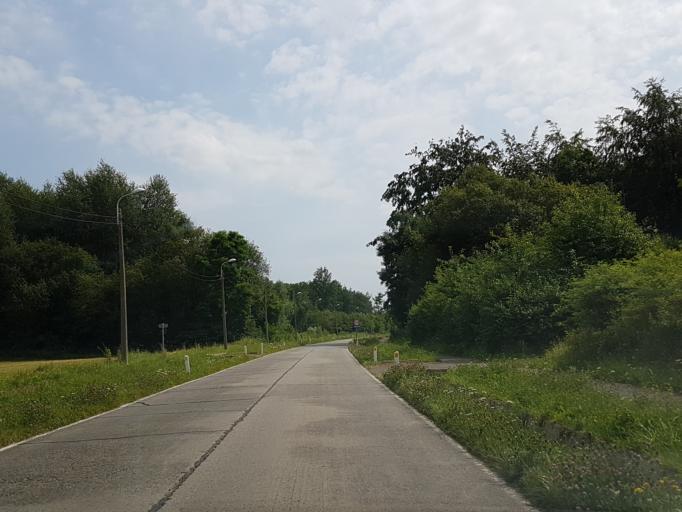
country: BE
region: Flanders
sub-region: Provincie Vlaams-Brabant
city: Herent
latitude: 50.9159
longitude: 4.6383
